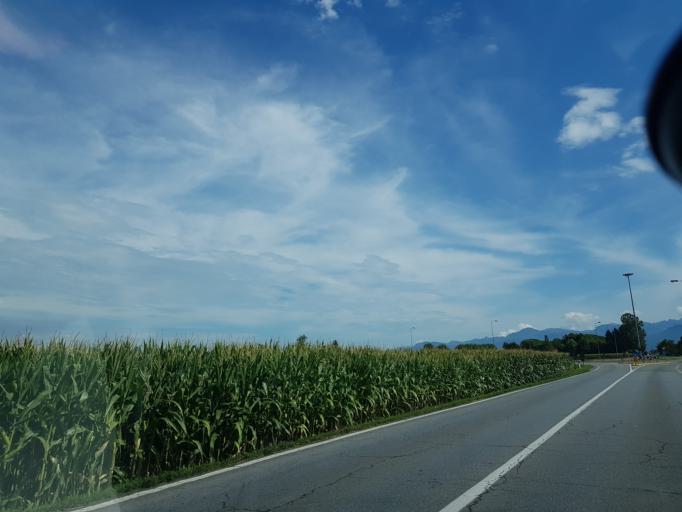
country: IT
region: Piedmont
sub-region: Provincia di Cuneo
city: Roata Rossi
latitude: 44.4487
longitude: 7.5266
